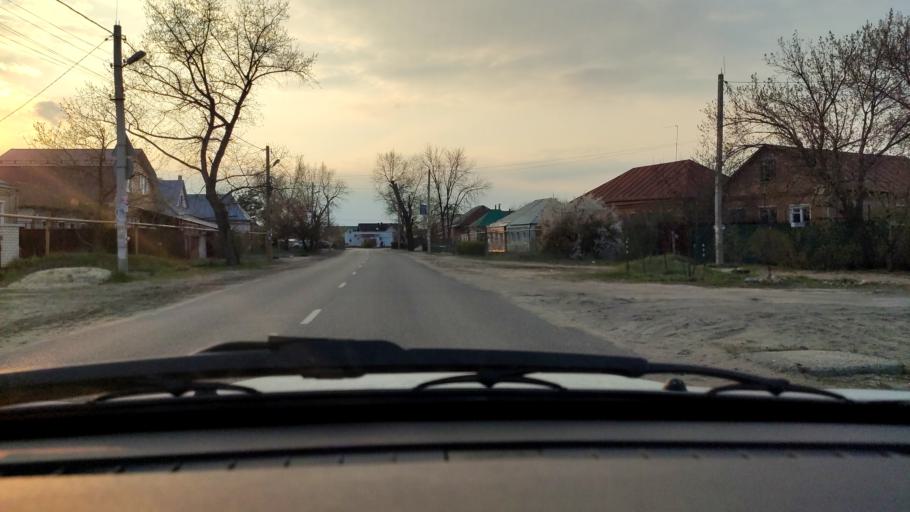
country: RU
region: Voronezj
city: Somovo
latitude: 51.7479
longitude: 39.3371
